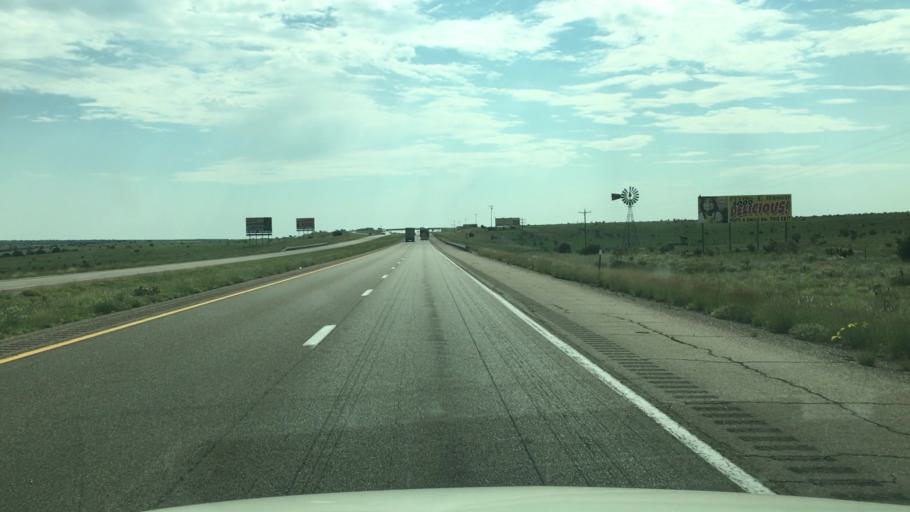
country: US
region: New Mexico
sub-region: San Miguel County
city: Las Vegas
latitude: 34.9962
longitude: -105.3957
